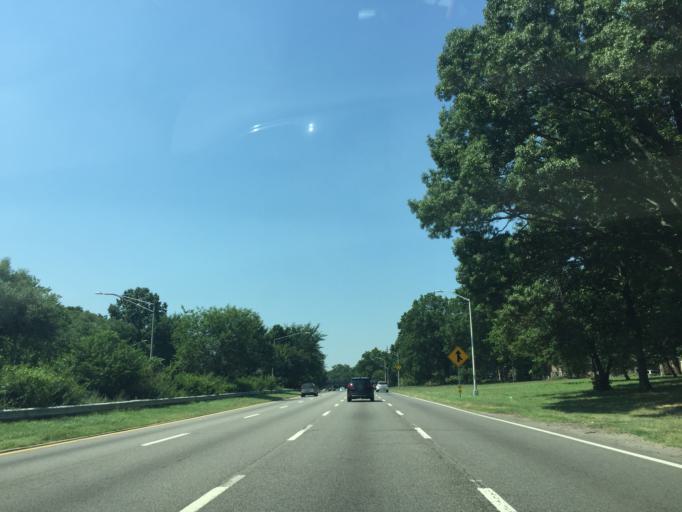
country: US
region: New York
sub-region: Nassau County
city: South Valley Stream
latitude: 40.6763
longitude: -73.7325
